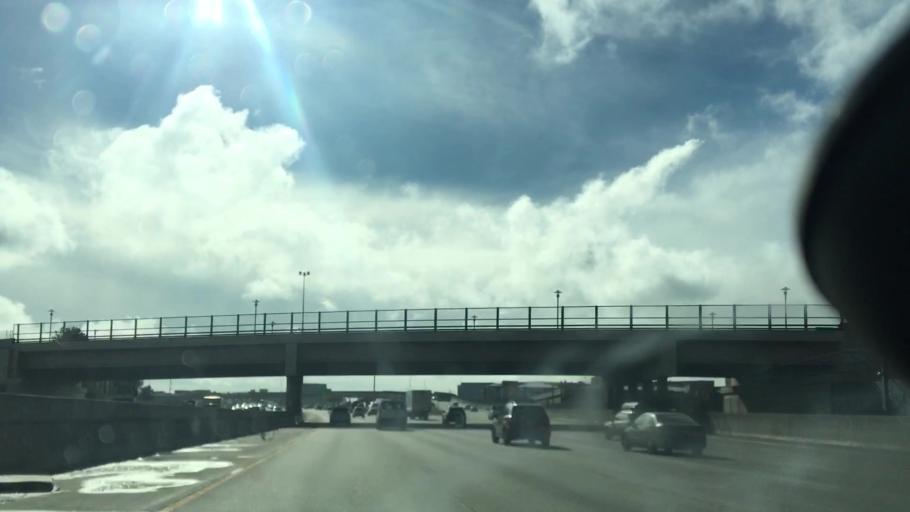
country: US
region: Colorado
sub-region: Arapahoe County
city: Greenwood Village
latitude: 39.6396
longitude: -104.9109
